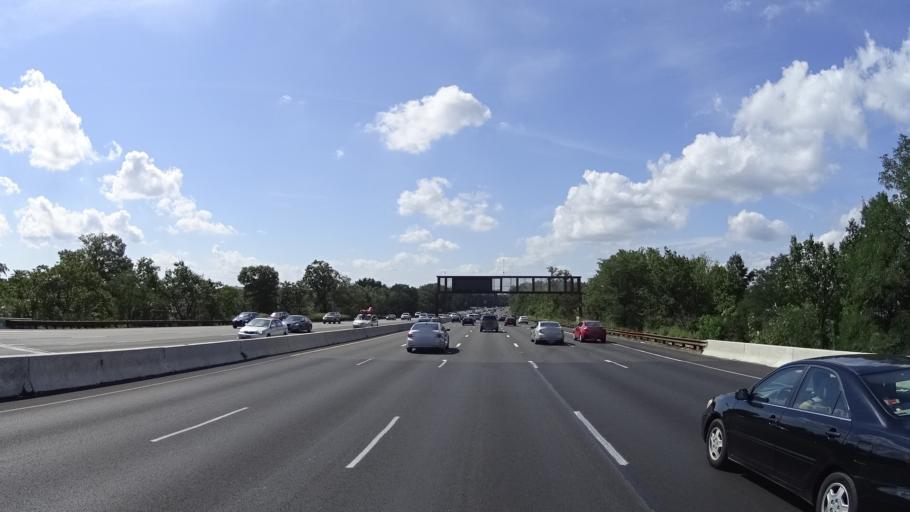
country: US
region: New Jersey
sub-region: Union County
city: Winfield
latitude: 40.6520
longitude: -74.2874
